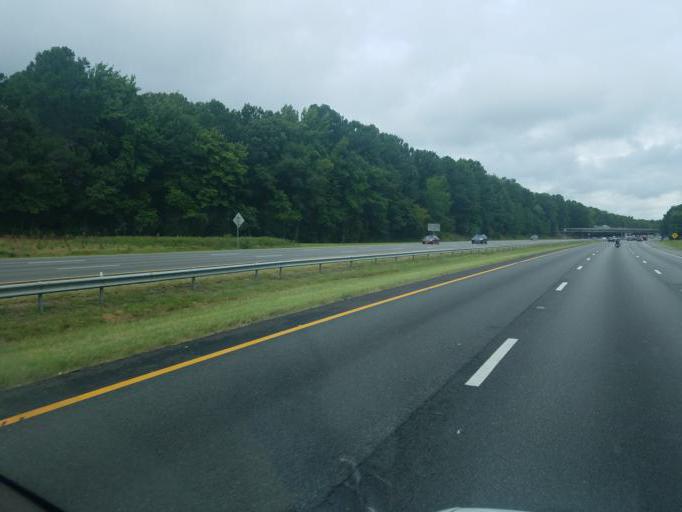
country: US
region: Virginia
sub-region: Henrico County
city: Chamberlayne
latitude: 37.6369
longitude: -77.4518
